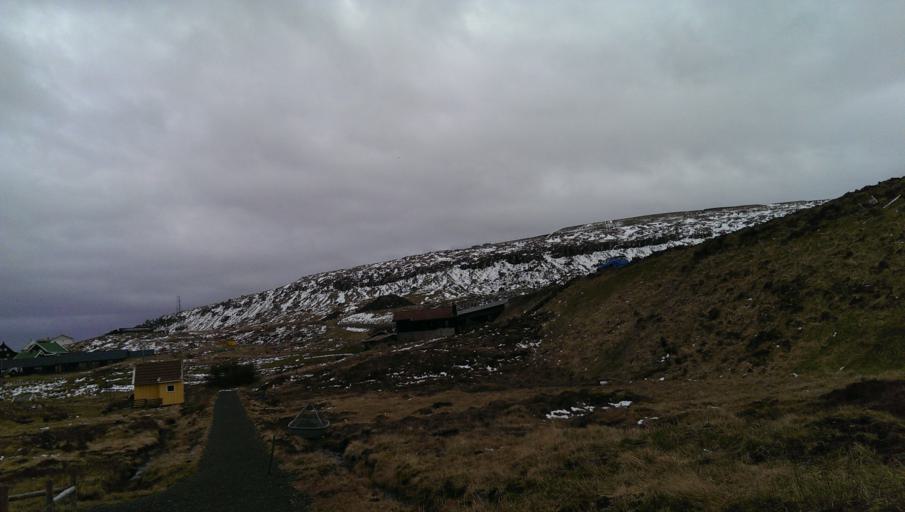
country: FO
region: Streymoy
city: Hoyvik
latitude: 62.0325
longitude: -6.7956
